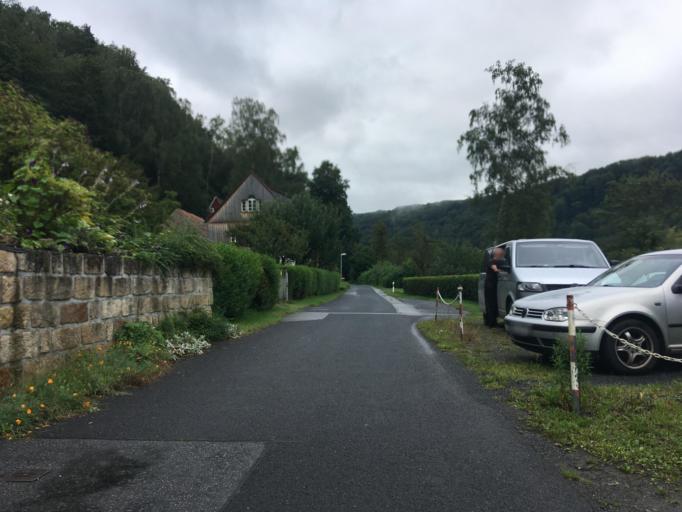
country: DE
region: Saxony
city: Struppen
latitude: 50.9483
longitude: 13.9989
